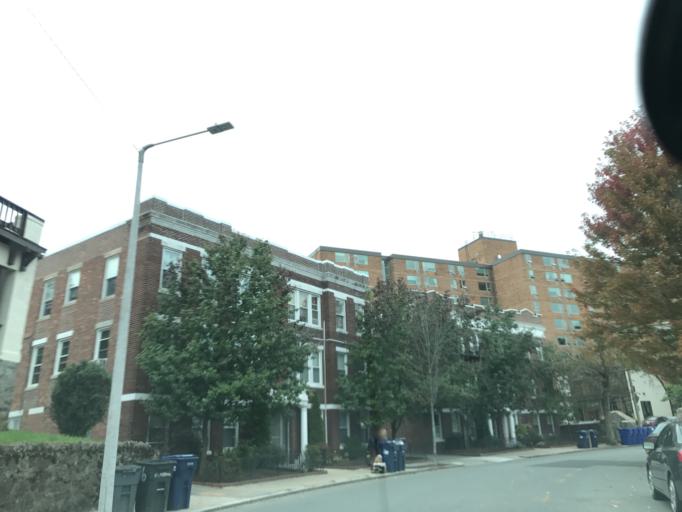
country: US
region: Massachusetts
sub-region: Norfolk County
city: Brookline
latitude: 42.3415
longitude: -71.1514
